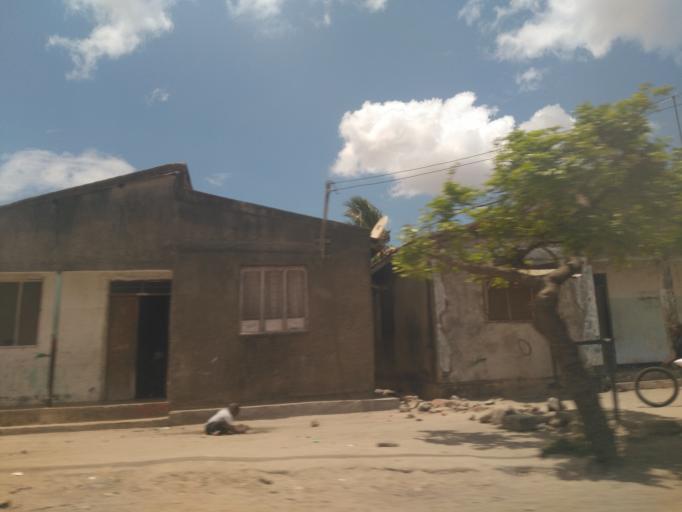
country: TZ
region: Dar es Salaam
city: Dar es Salaam
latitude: -6.8734
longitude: 39.2392
